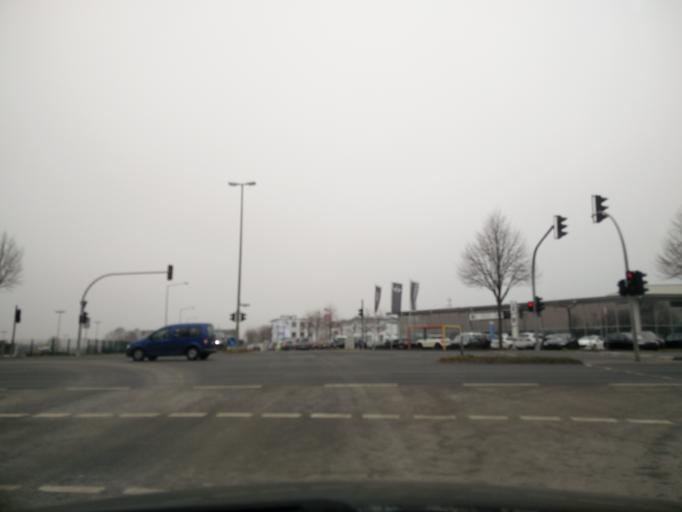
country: DE
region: North Rhine-Westphalia
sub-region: Regierungsbezirk Detmold
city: Paderborn
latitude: 51.7293
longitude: 8.7203
